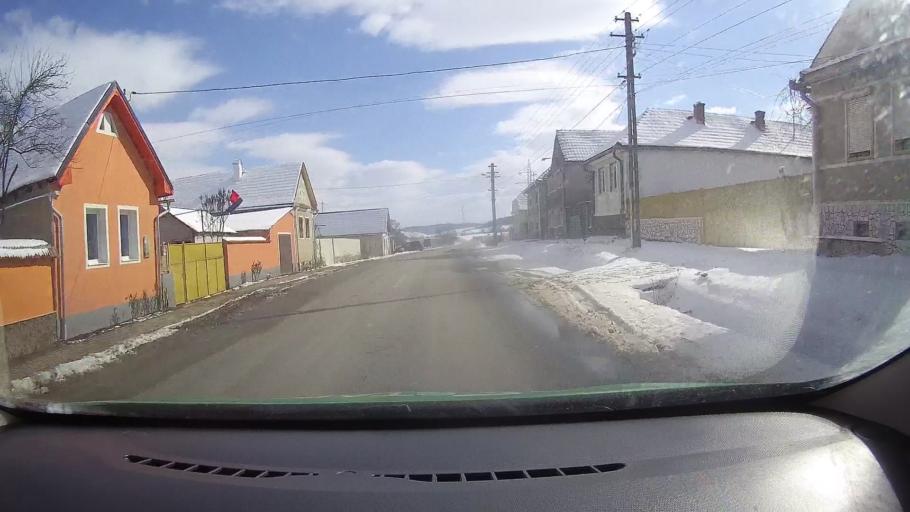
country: RO
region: Sibiu
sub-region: Comuna Barghis
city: Barghis
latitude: 45.9797
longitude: 24.5405
